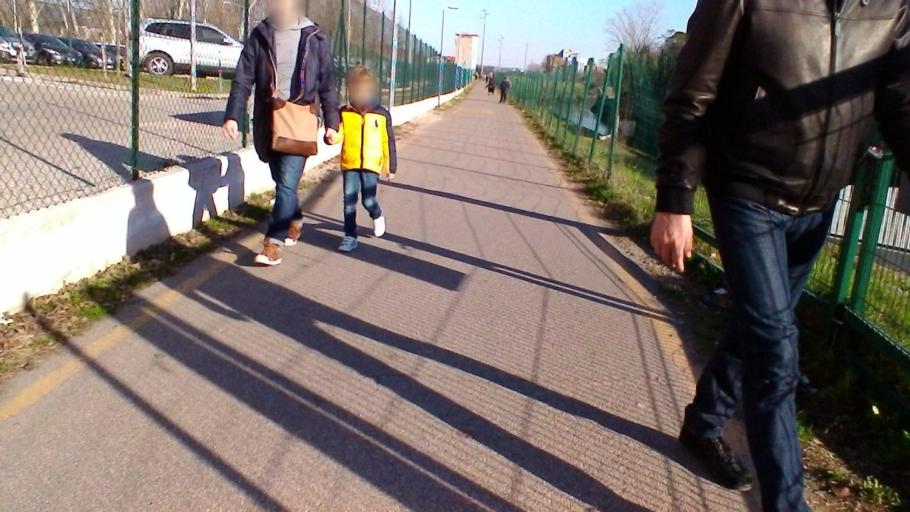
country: IT
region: Veneto
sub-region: Provincia di Verona
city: Parona
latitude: 45.4583
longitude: 10.9519
